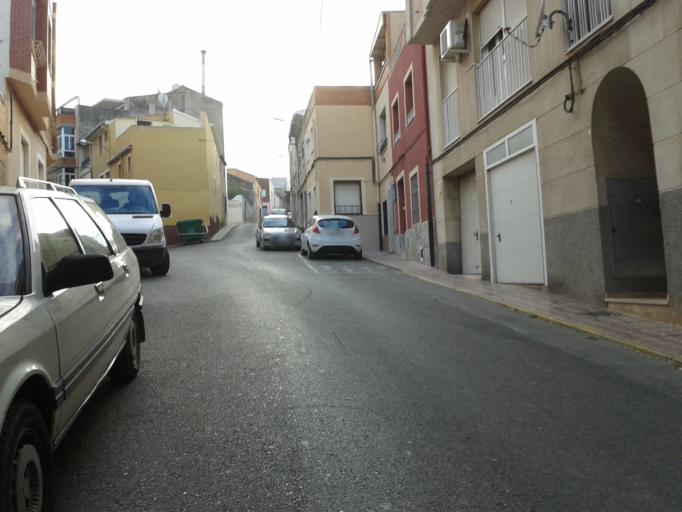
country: ES
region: Castille-La Mancha
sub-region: Provincia de Albacete
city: Caudete
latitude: 38.7059
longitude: -0.9896
